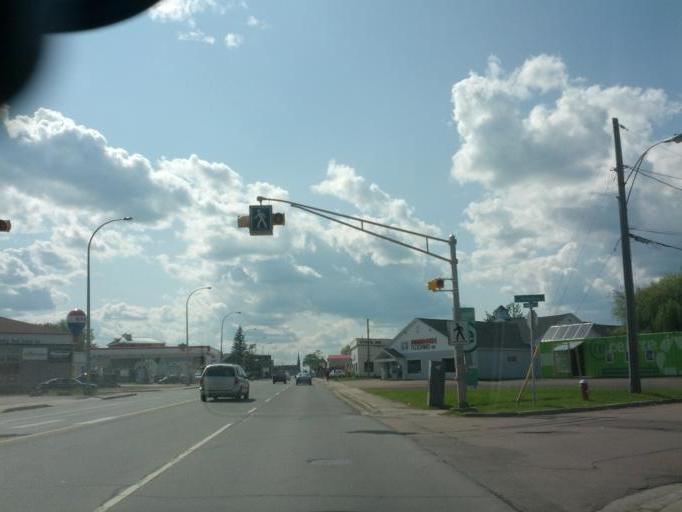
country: CA
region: New Brunswick
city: Moncton
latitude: 46.0981
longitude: -64.7980
